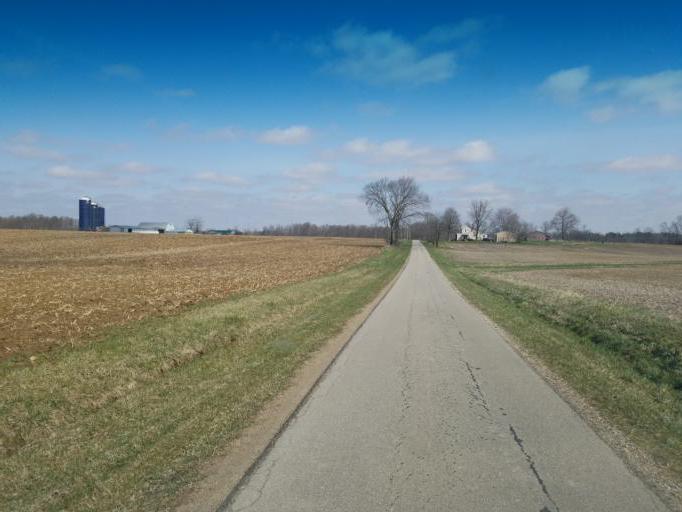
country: US
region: Ohio
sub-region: Crawford County
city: Bucyrus
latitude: 40.9243
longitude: -83.0598
